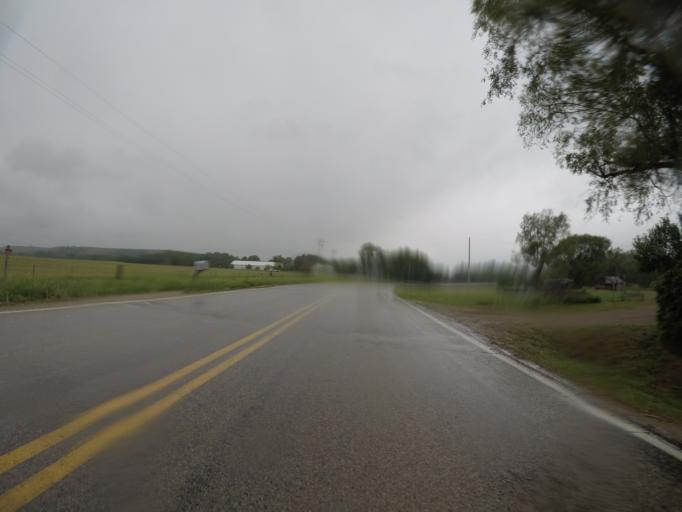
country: US
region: Kansas
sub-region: Pottawatomie County
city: Westmoreland
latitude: 39.3999
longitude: -96.1838
